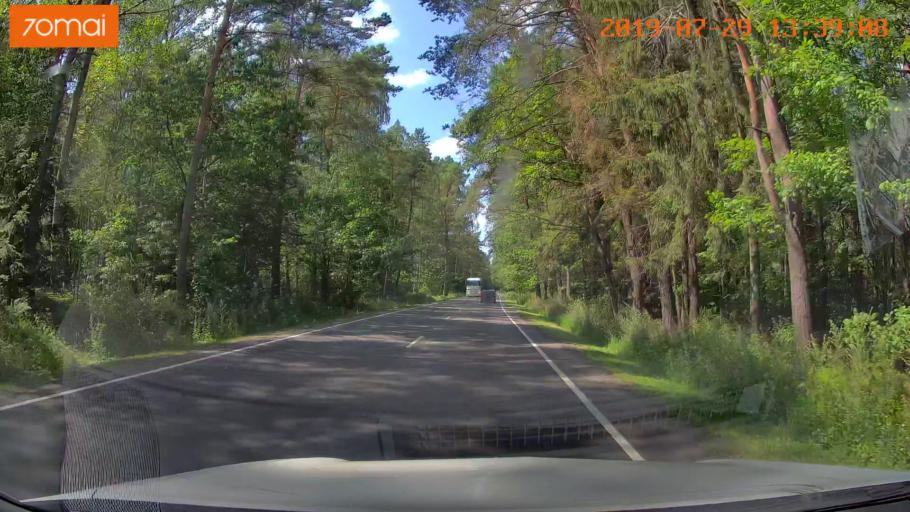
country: RU
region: Kaliningrad
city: Svetlyy
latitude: 54.7233
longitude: 20.1587
